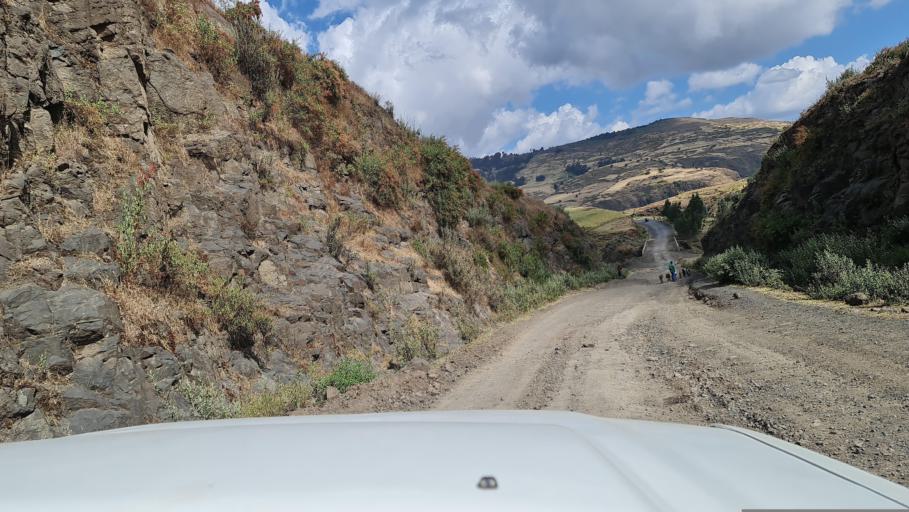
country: ET
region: Amhara
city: Debark'
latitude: 13.1330
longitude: 37.9273
